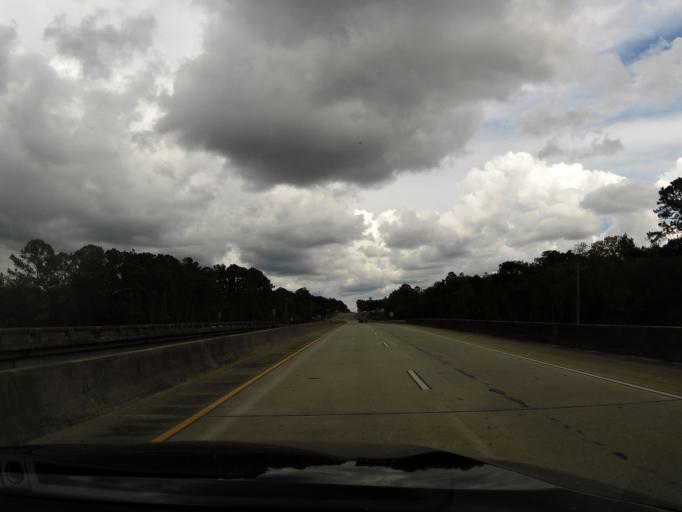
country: US
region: Georgia
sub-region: Brantley County
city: Nahunta
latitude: 31.2203
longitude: -81.8621
